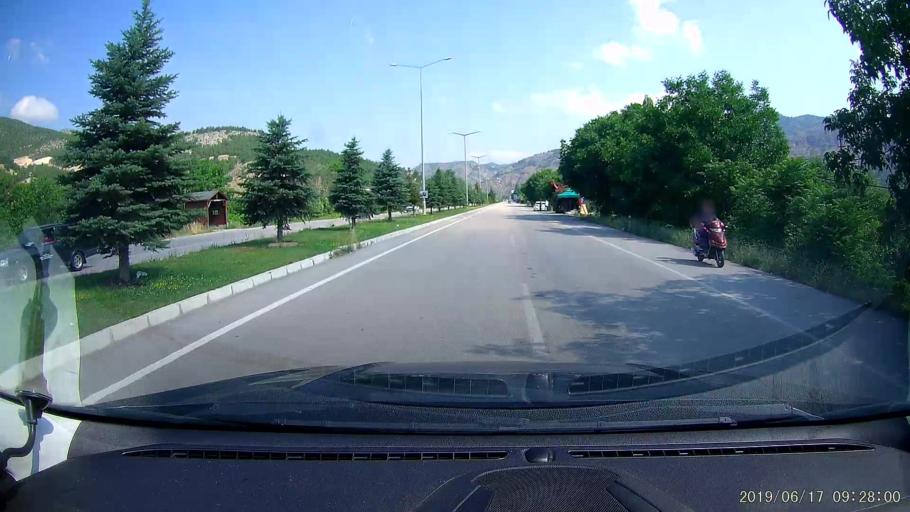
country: TR
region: Amasya
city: Amasya
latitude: 40.6833
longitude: 35.8235
